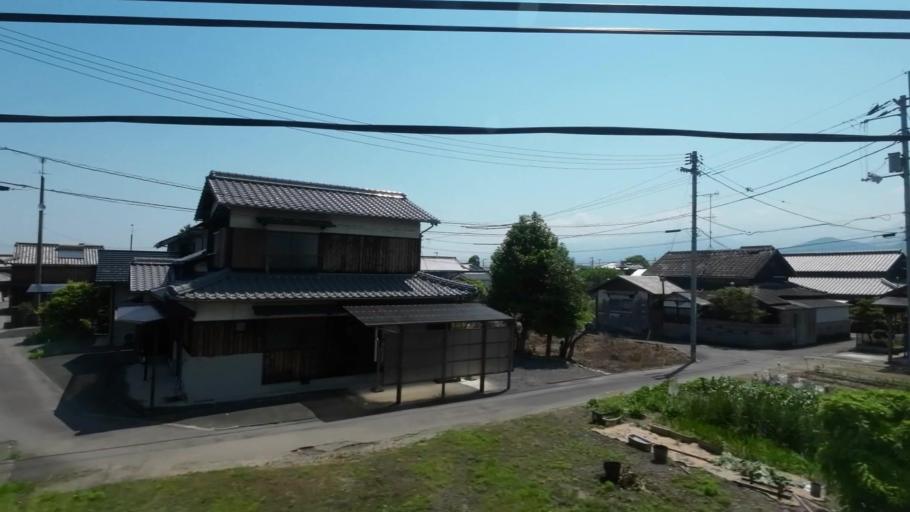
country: JP
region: Ehime
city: Saijo
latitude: 33.9111
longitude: 133.0991
